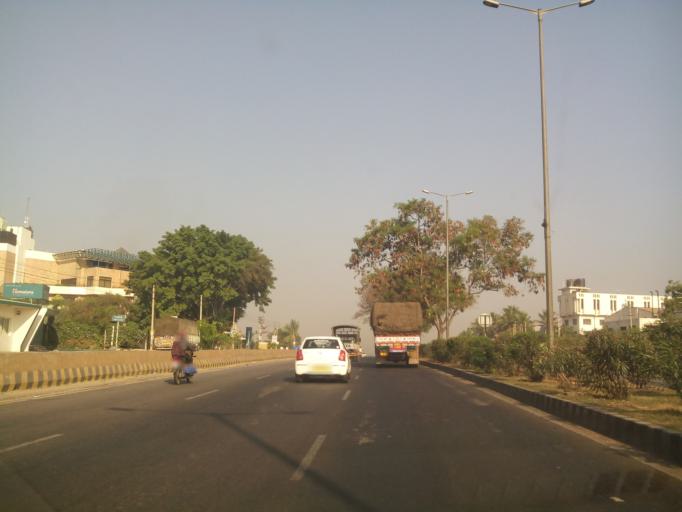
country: IN
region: Karnataka
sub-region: Bangalore Rural
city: Nelamangala
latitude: 13.0660
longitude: 77.4529
